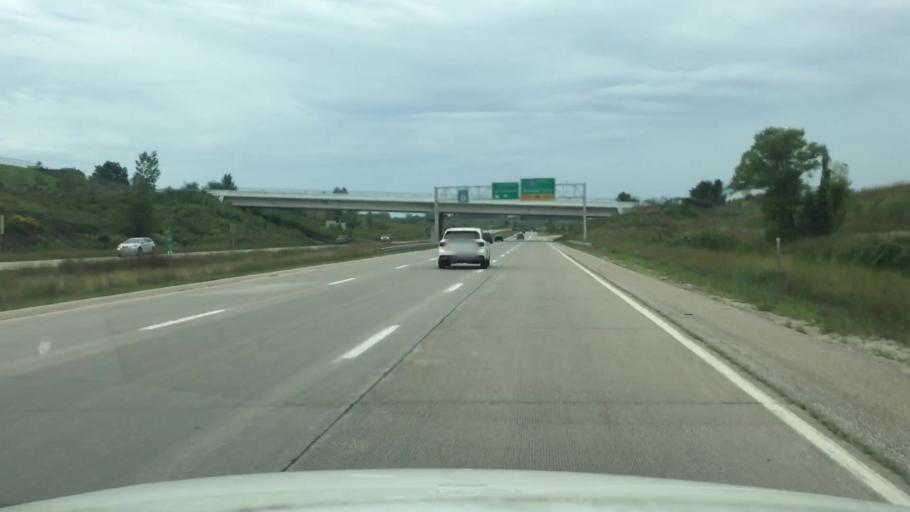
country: US
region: Iowa
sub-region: Polk County
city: West Des Moines
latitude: 41.5230
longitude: -93.7588
